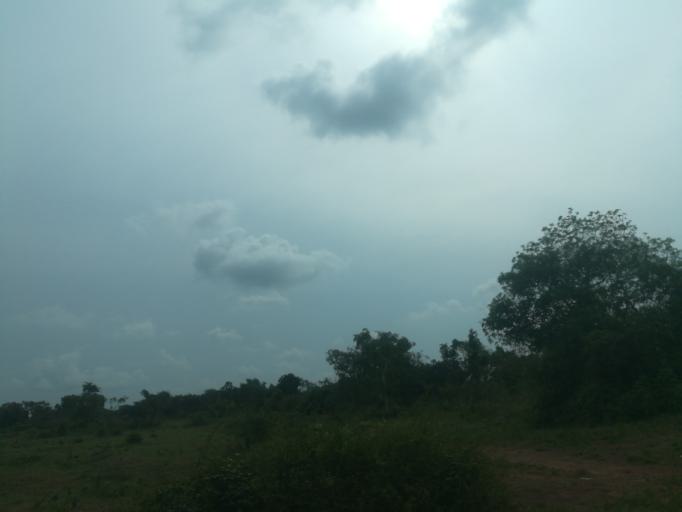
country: NG
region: Ogun
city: Ayetoro
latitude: 7.2751
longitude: 3.0983
